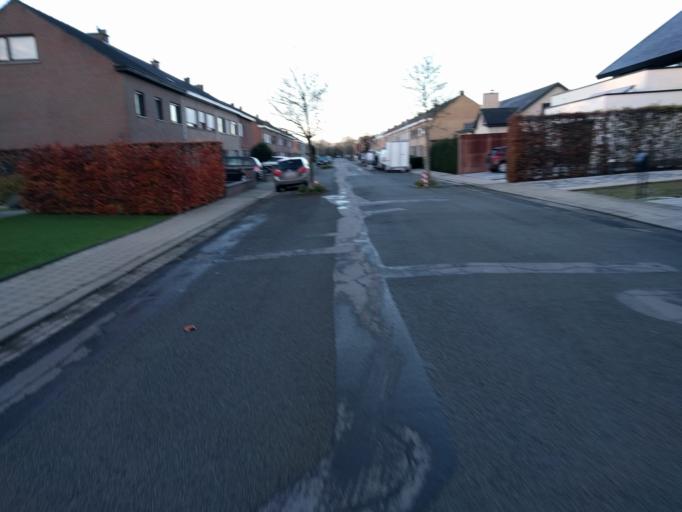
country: BE
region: Flanders
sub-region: Provincie West-Vlaanderen
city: Wevelgem
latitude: 50.8100
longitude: 3.1778
